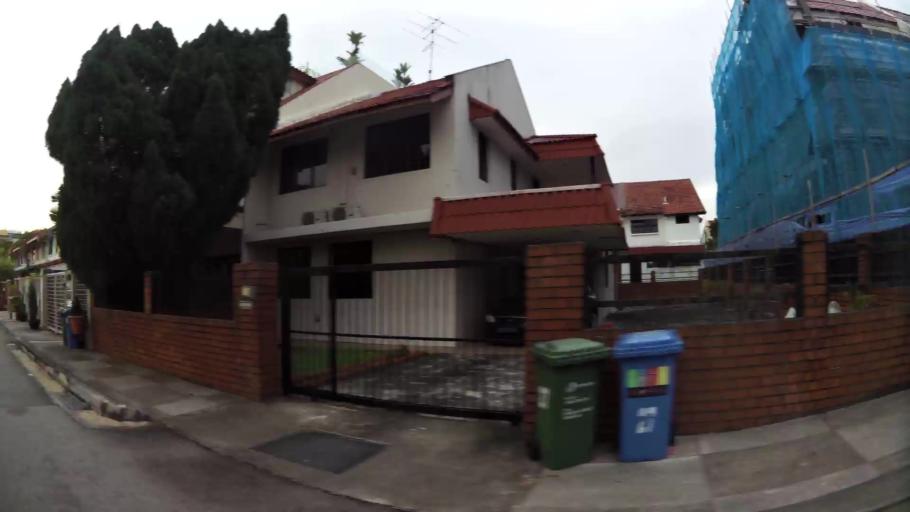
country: SG
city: Singapore
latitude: 1.3332
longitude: 103.8766
